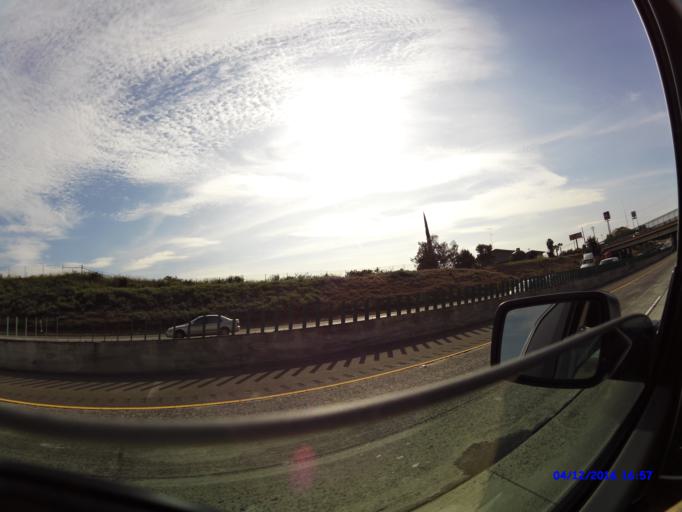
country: US
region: California
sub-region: Stanislaus County
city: Modesto
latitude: 37.6452
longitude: -121.0157
